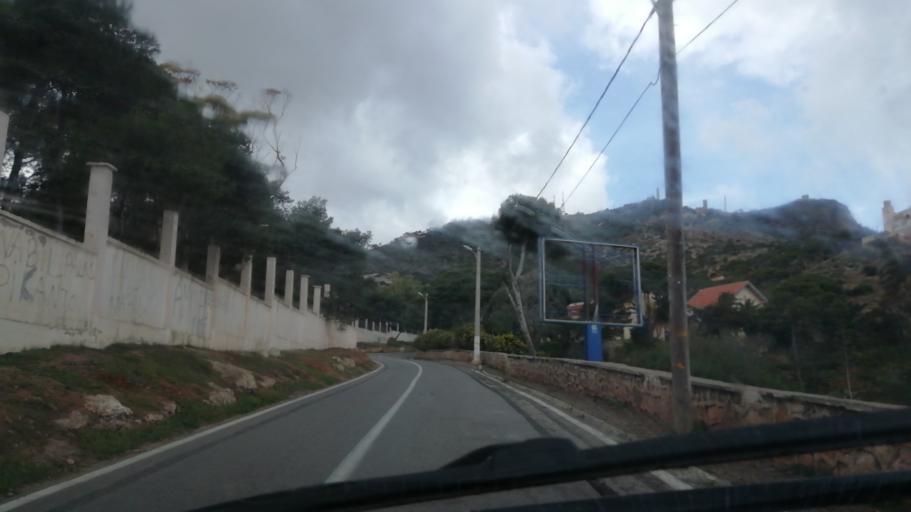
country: DZ
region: Oran
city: Oran
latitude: 35.7020
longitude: -0.6610
